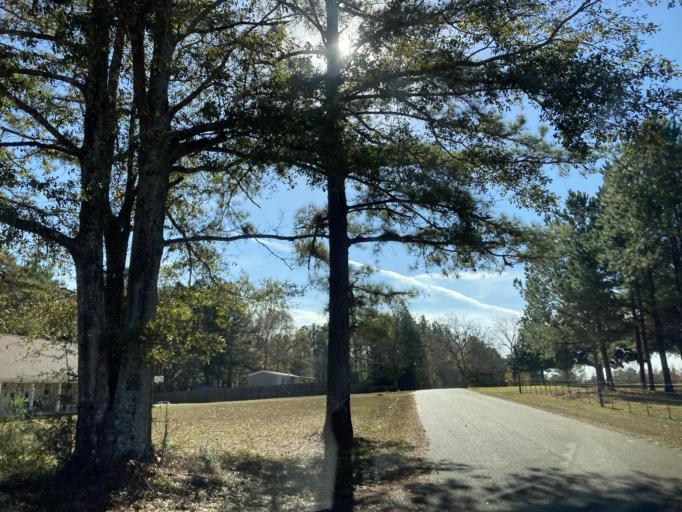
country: US
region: Mississippi
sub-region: Lamar County
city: Sumrall
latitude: 31.2645
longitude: -89.5279
